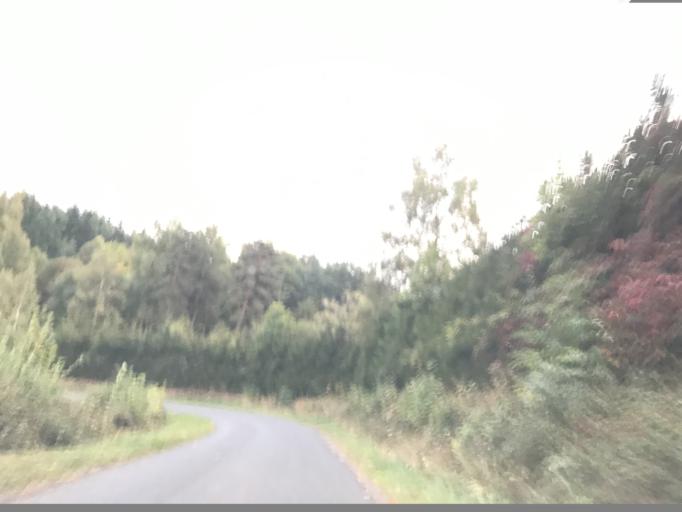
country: FR
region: Auvergne
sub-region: Departement du Puy-de-Dome
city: La Monnerie-le-Montel
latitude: 45.8414
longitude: 3.6114
